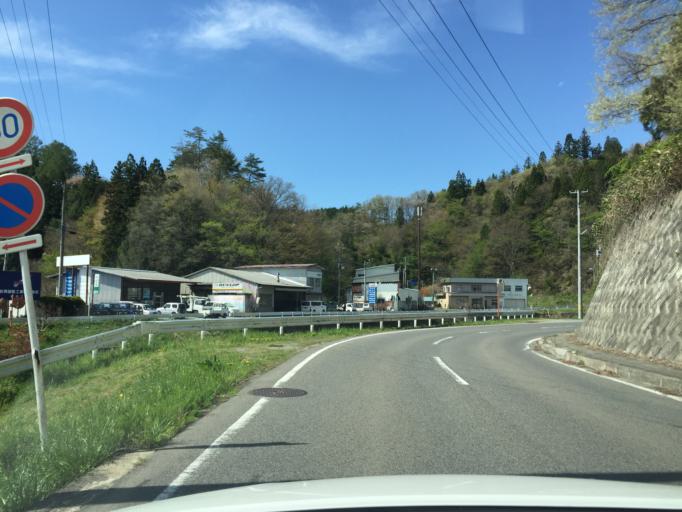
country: JP
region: Fukushima
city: Funehikimachi-funehiki
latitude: 37.5309
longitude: 140.6110
